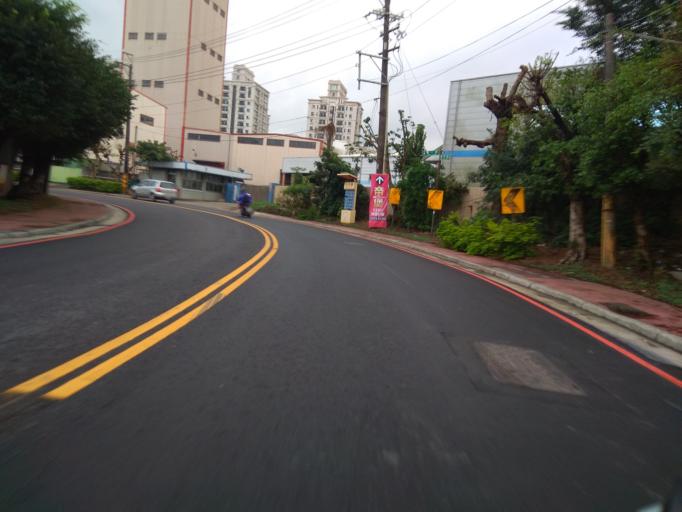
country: TW
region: Taiwan
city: Daxi
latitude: 24.9229
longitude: 121.1719
